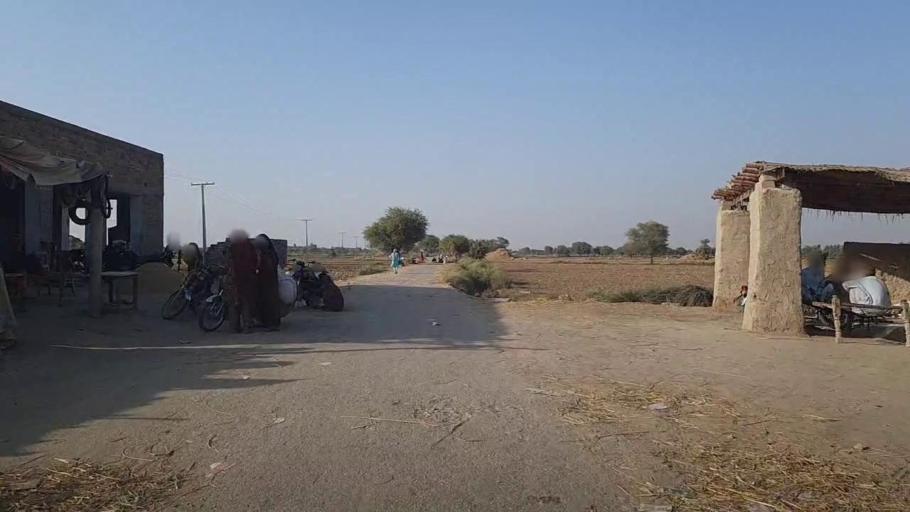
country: PK
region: Sindh
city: Kashmor
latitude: 28.4136
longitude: 69.4112
